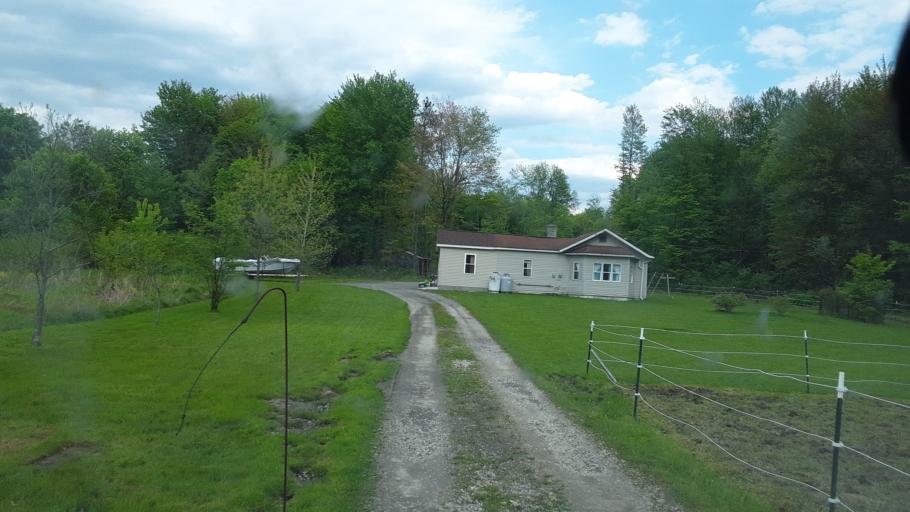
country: US
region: Ohio
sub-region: Portage County
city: Garrettsville
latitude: 41.3146
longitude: -81.0505
